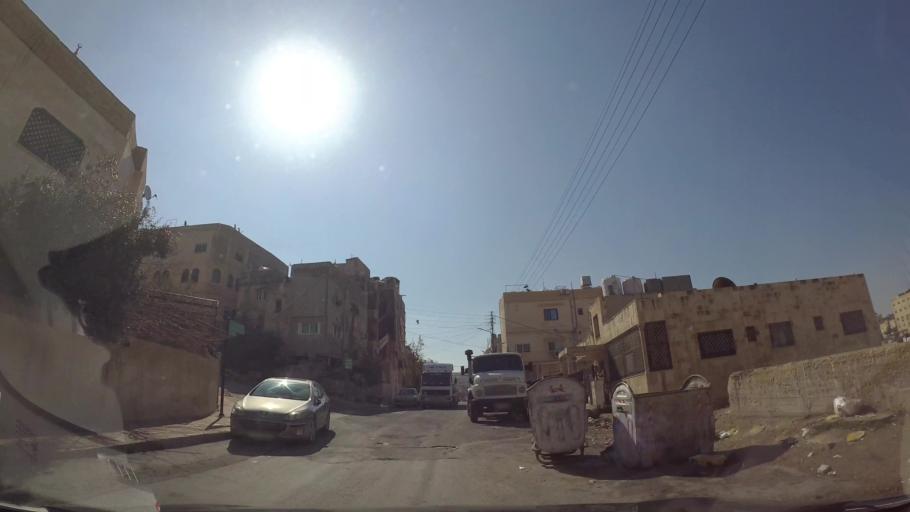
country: JO
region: Amman
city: Amman
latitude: 31.9890
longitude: 35.9837
